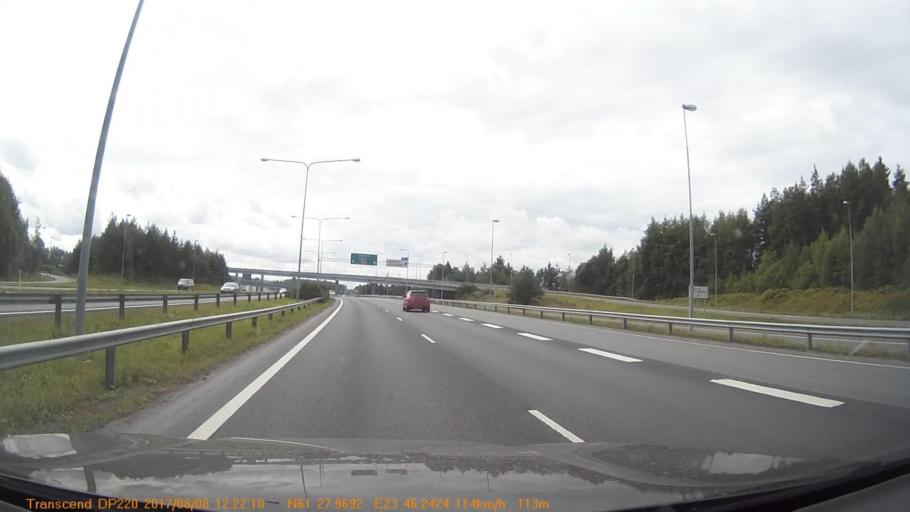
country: FI
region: Pirkanmaa
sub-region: Tampere
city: Tampere
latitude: 61.4660
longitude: 23.7705
